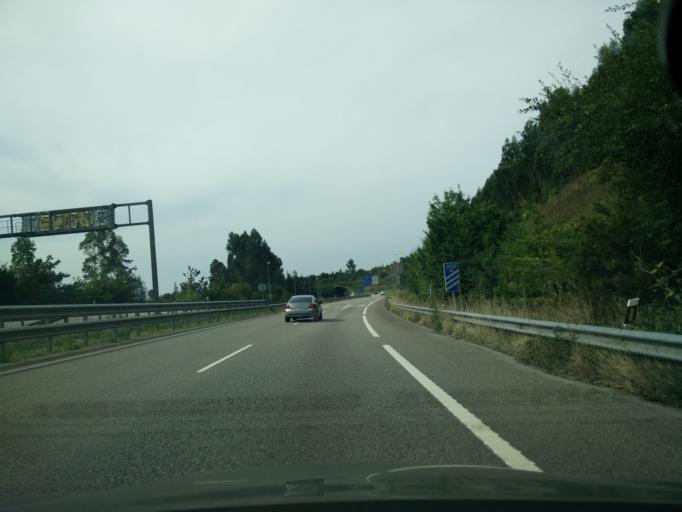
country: ES
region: Asturias
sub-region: Province of Asturias
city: Arriba
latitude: 43.5065
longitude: -5.5946
